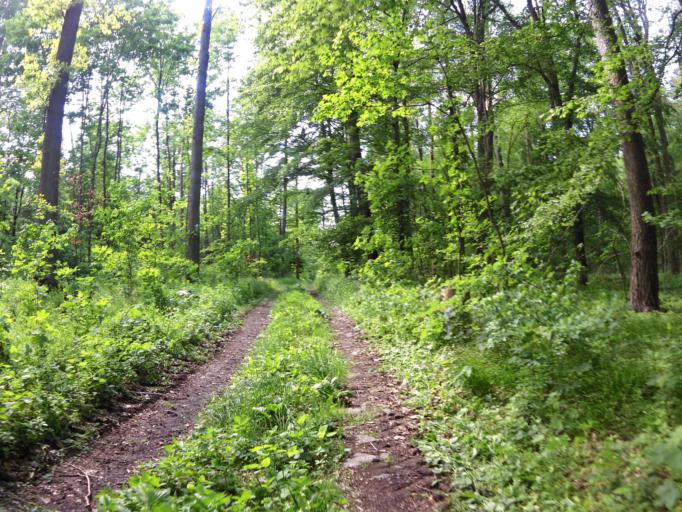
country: DE
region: Bavaria
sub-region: Regierungsbezirk Unterfranken
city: Reichenberg
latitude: 49.7505
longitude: 9.9228
